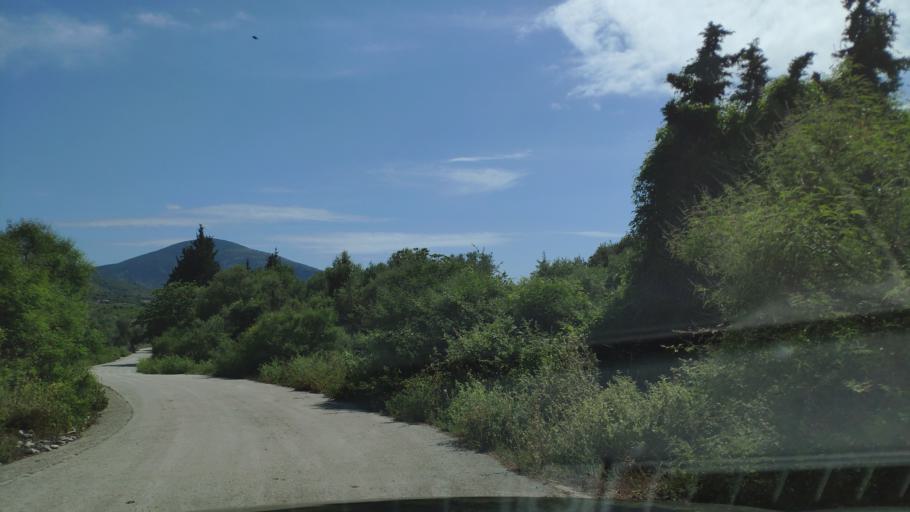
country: AL
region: Vlore
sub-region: Rrethi i Sarandes
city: Konispol
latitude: 39.6227
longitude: 20.2010
